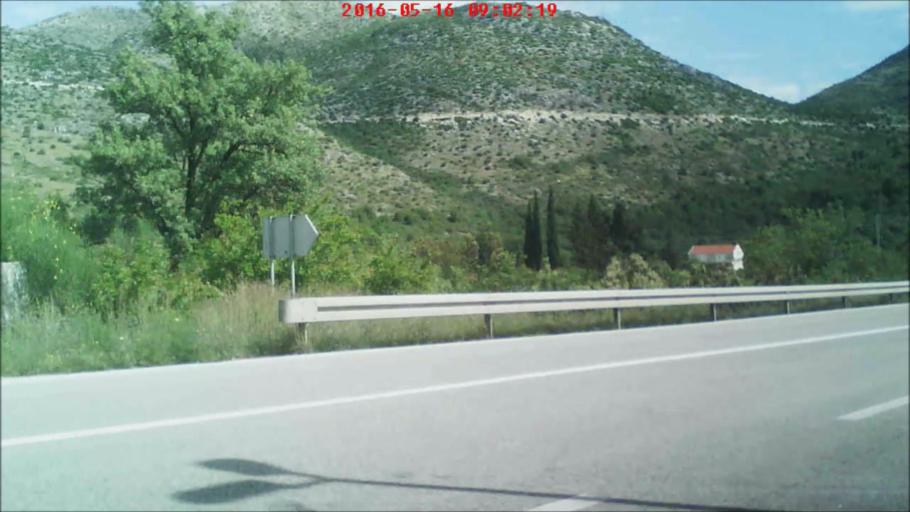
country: HR
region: Dubrovacko-Neretvanska
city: Podgora
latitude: 42.7888
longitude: 17.8788
